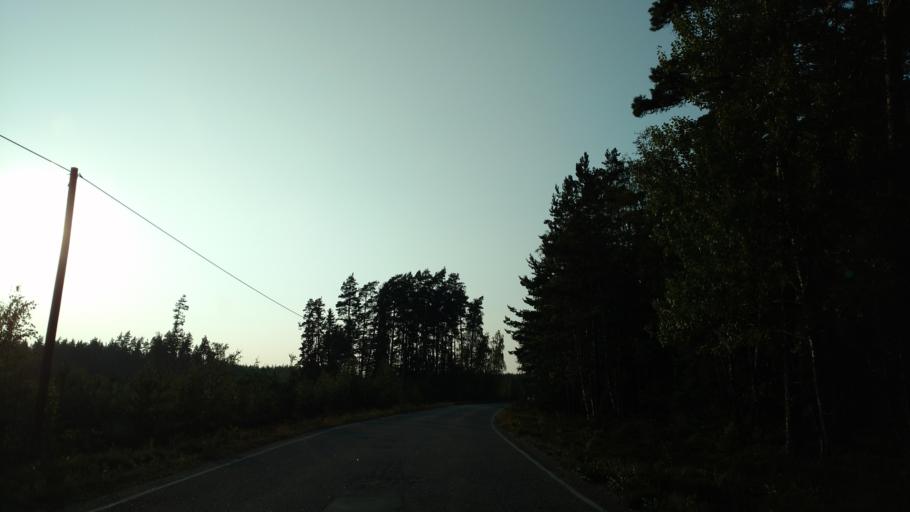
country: FI
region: Varsinais-Suomi
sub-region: Salo
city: Saerkisalo
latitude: 60.1923
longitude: 22.9473
